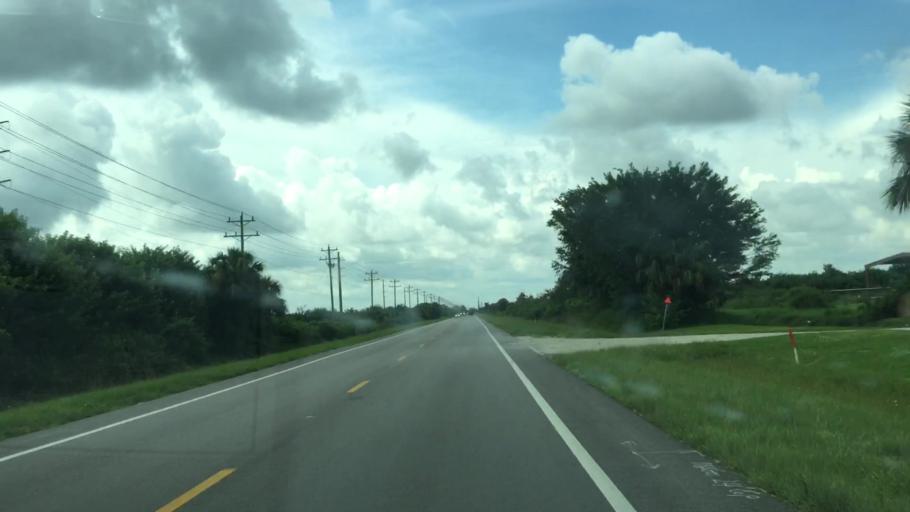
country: US
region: Florida
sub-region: Collier County
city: Immokalee
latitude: 26.3862
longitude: -81.4171
